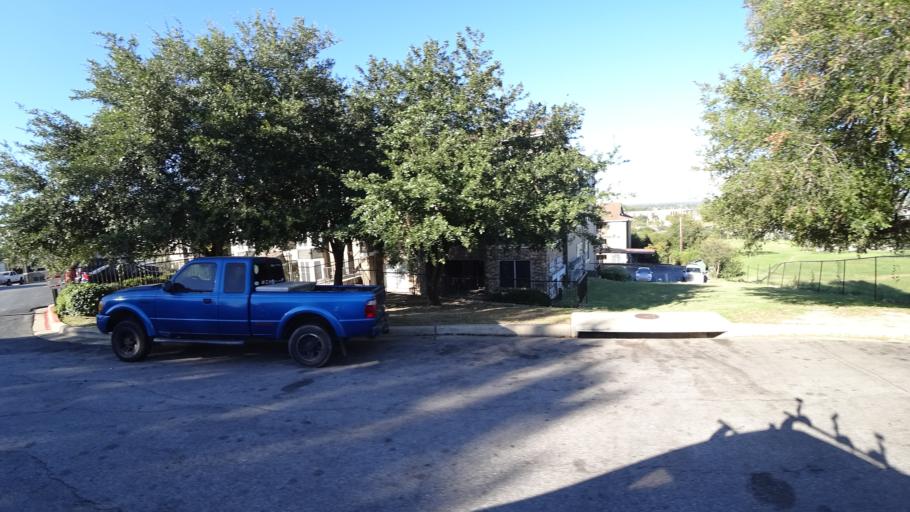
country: US
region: Texas
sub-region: Travis County
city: Austin
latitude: 30.2338
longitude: -97.7261
